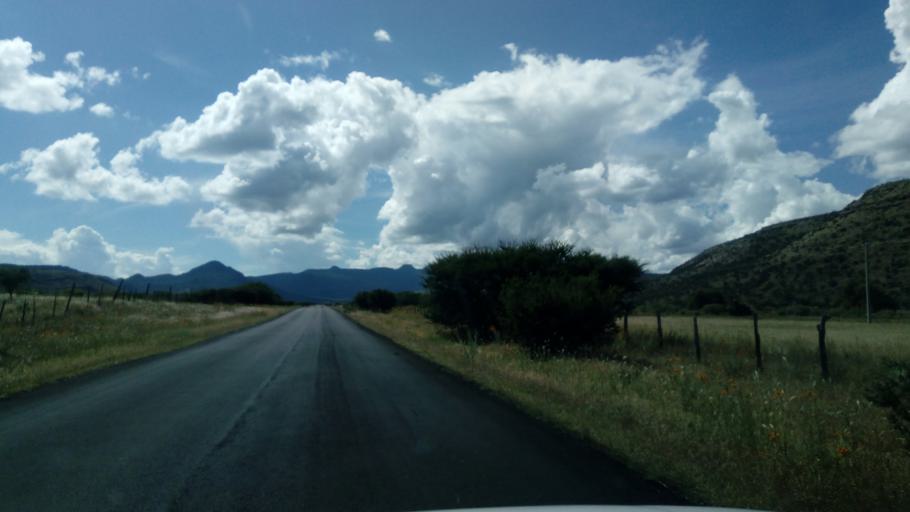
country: MX
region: Durango
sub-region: Durango
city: Jose Refugio Salcido
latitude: 23.8147
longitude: -104.4834
